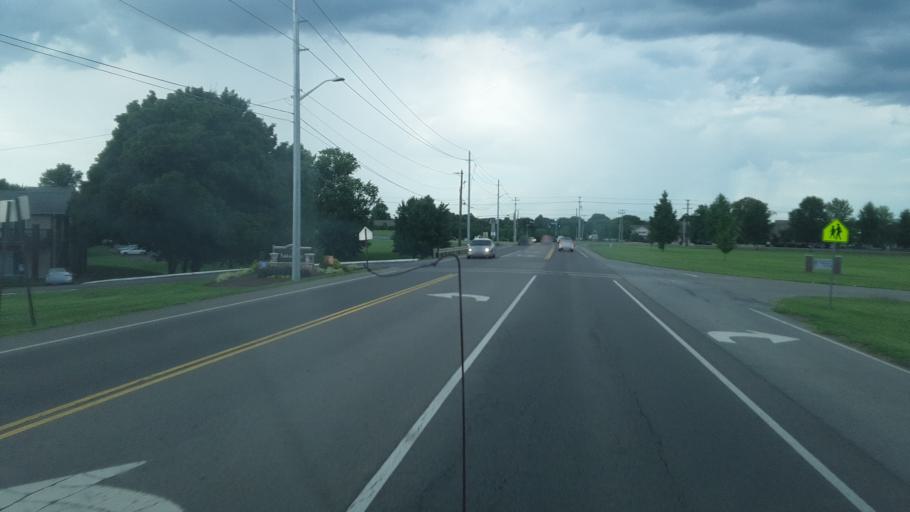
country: US
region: Tennessee
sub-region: Montgomery County
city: Clarksville
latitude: 36.5192
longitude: -87.2780
